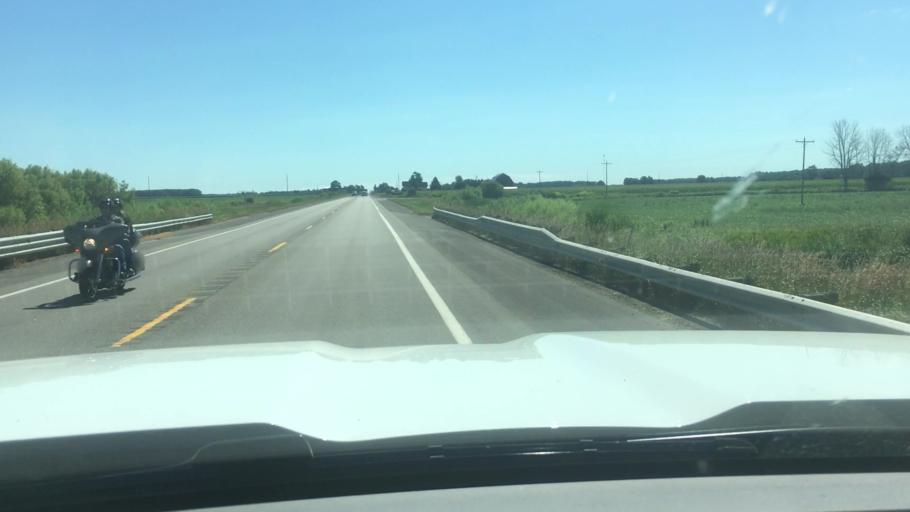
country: US
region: Michigan
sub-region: Montcalm County
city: Carson City
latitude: 43.1766
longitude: -84.7907
